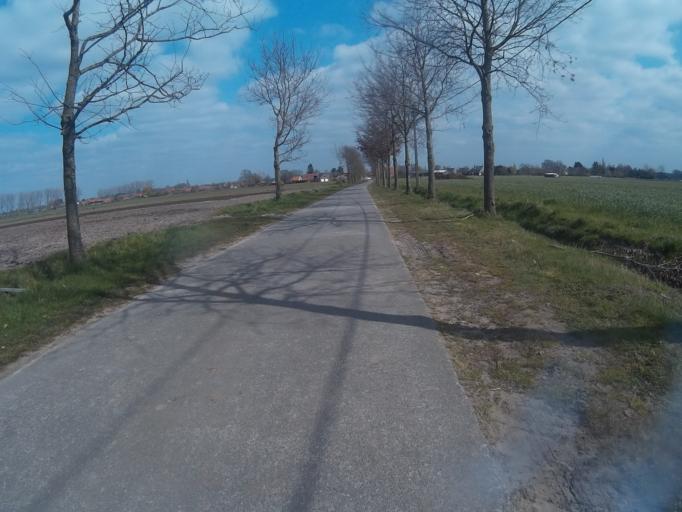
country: BE
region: Flanders
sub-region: Provincie Oost-Vlaanderen
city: Eeklo
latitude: 51.1533
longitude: 3.5053
